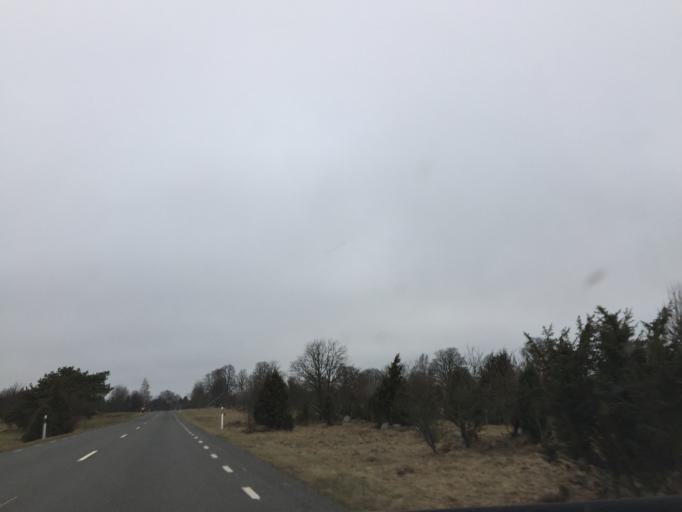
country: EE
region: Saare
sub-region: Kuressaare linn
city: Kuressaare
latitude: 58.5354
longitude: 22.3395
